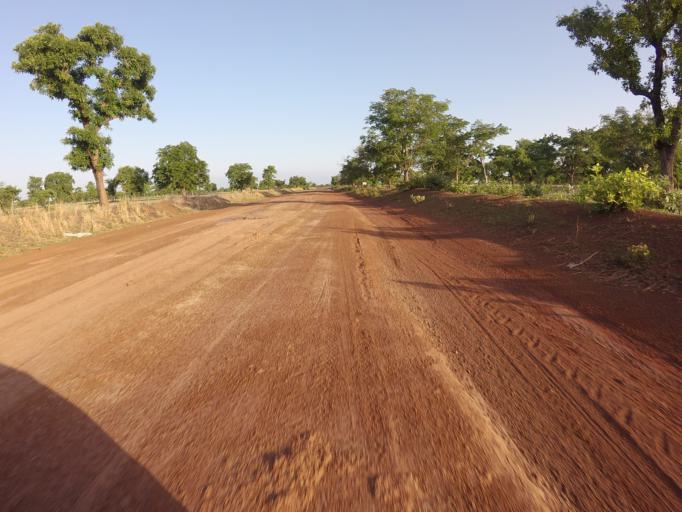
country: TG
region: Savanes
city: Sansanne-Mango
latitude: 10.2989
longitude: -0.0895
